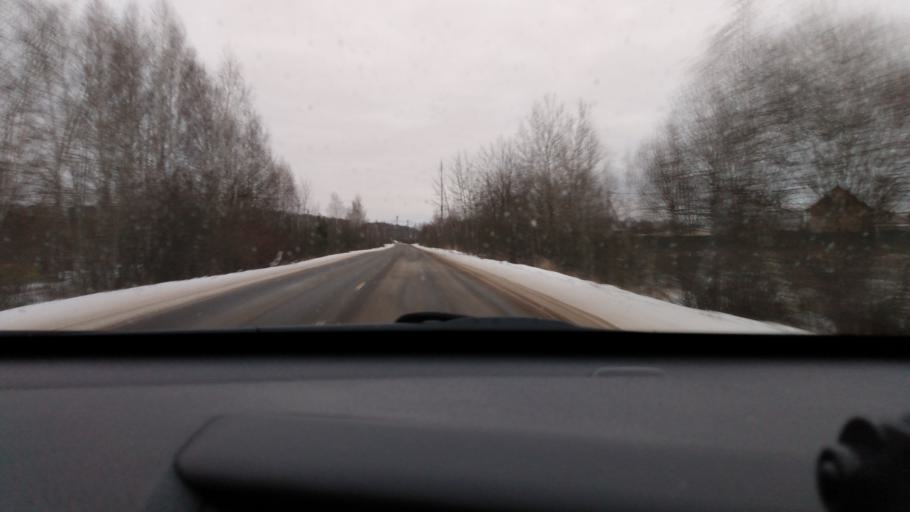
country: RU
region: Moskovskaya
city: Bronnitsy
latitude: 55.2905
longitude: 38.2439
